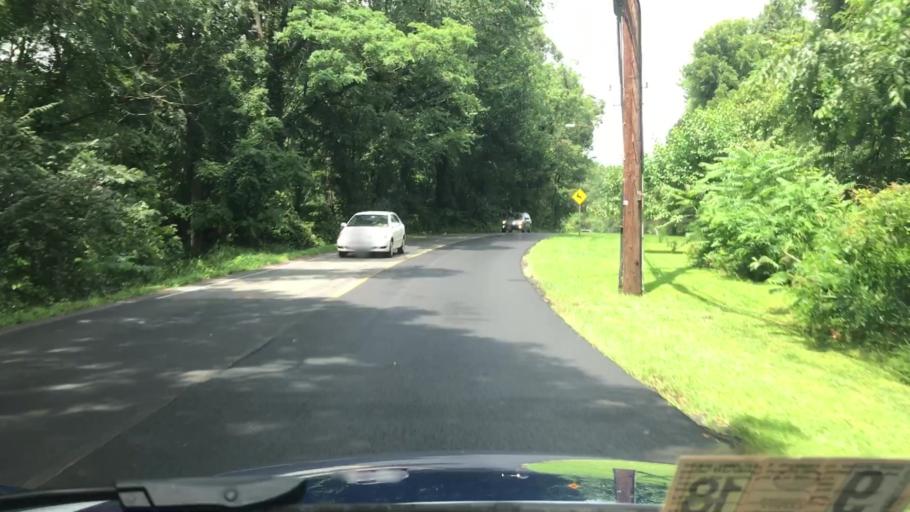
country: US
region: Virginia
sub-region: Fairfax County
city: Vienna
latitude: 38.9099
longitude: -77.2852
